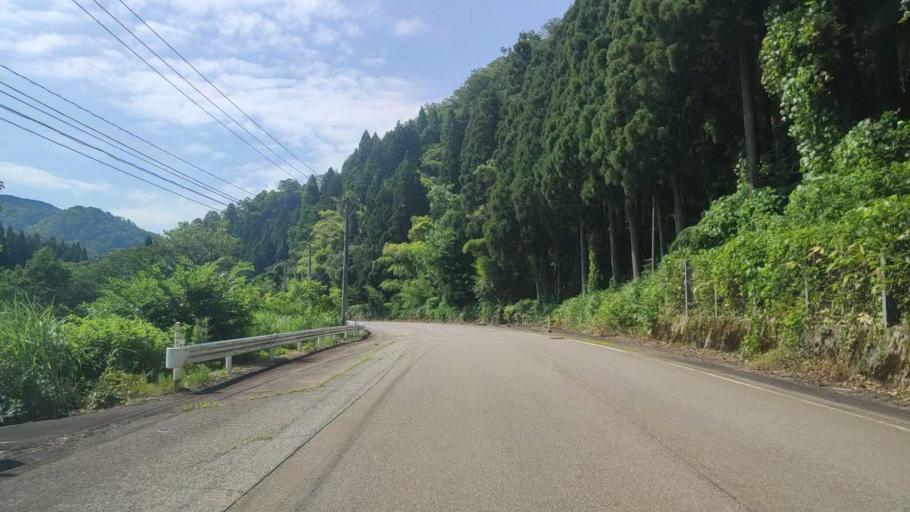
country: JP
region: Ishikawa
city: Komatsu
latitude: 36.3260
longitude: 136.5290
